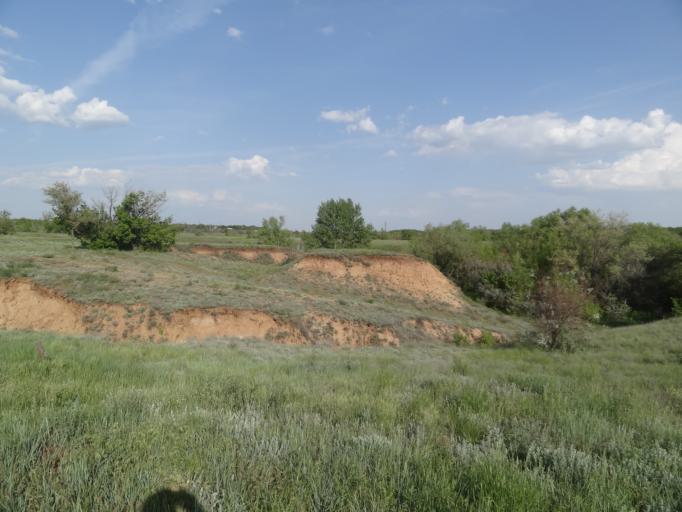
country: RU
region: Saratov
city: Privolzhskiy
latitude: 51.3501
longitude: 46.0444
